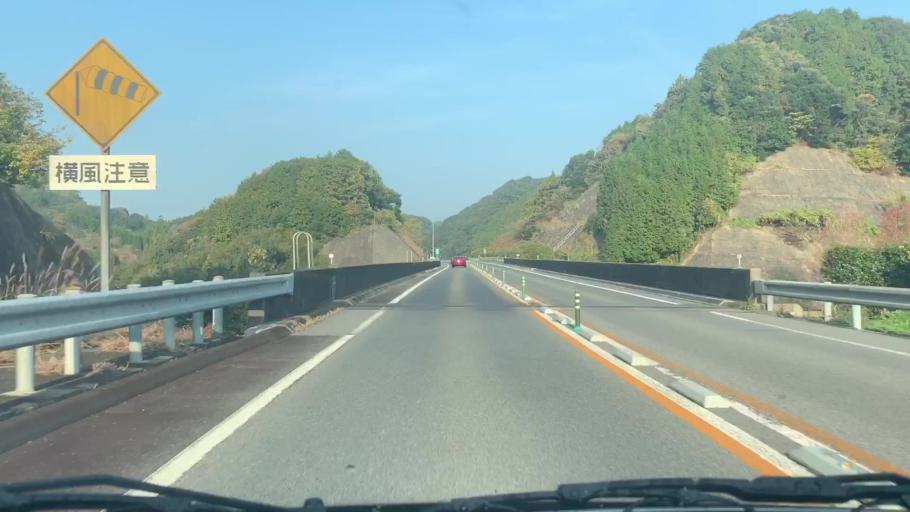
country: JP
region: Saga Prefecture
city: Ureshinomachi-shimojuku
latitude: 33.1452
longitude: 129.9517
